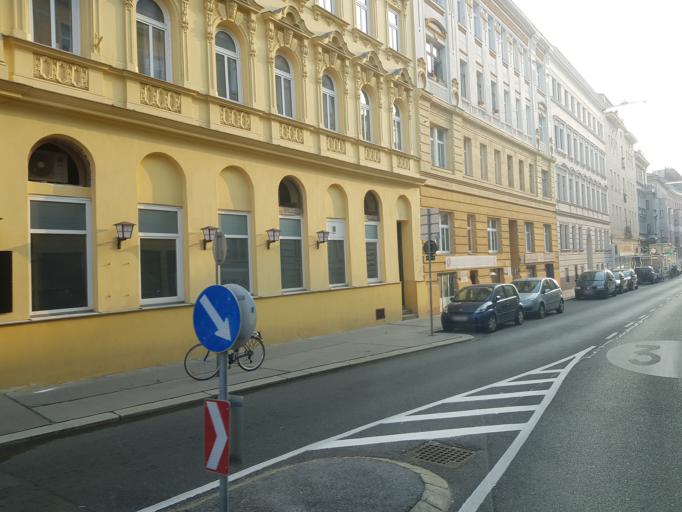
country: AT
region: Vienna
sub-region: Wien Stadt
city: Vienna
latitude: 48.2283
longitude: 16.3368
